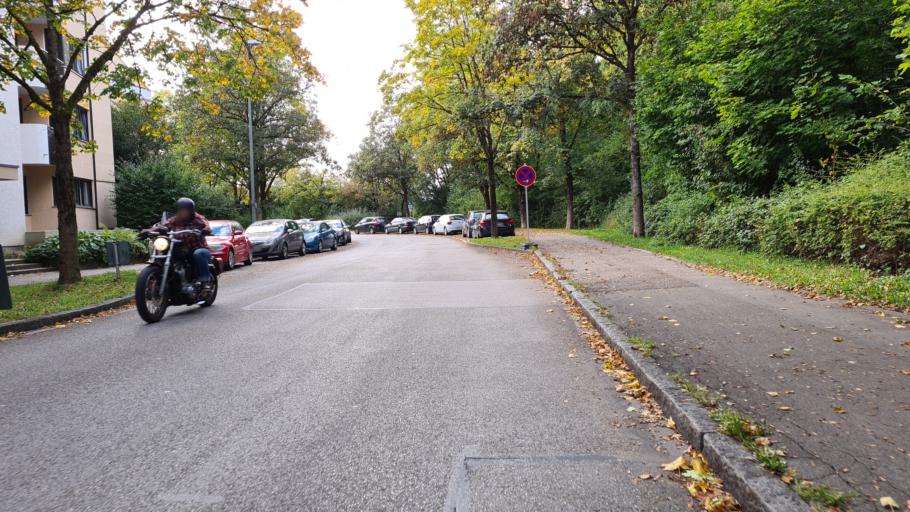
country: DE
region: Bavaria
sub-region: Upper Bavaria
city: Grafelfing
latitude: 48.1094
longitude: 11.4479
